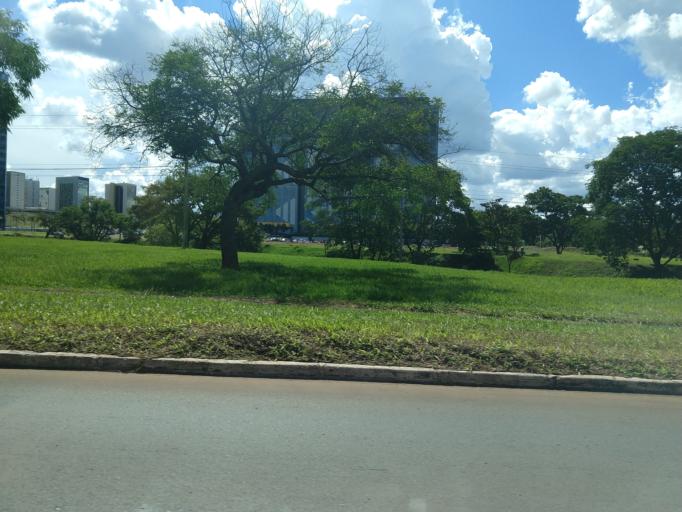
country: BR
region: Federal District
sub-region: Brasilia
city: Brasilia
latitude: -15.7843
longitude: -47.8738
